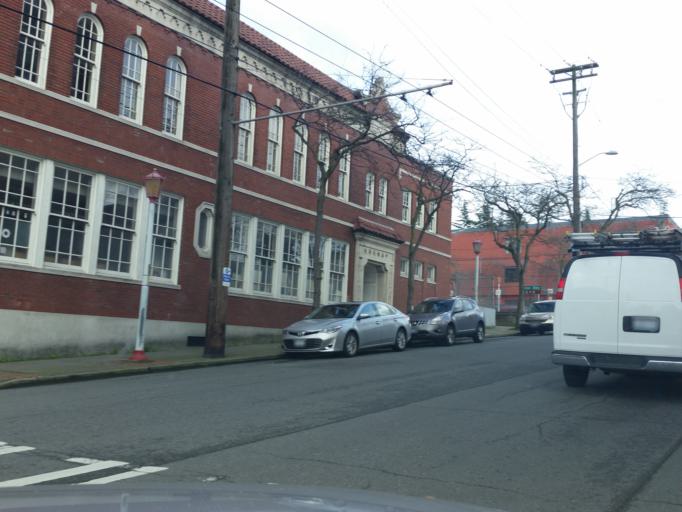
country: US
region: Washington
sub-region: King County
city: Seattle
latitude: 47.5975
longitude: -122.3236
